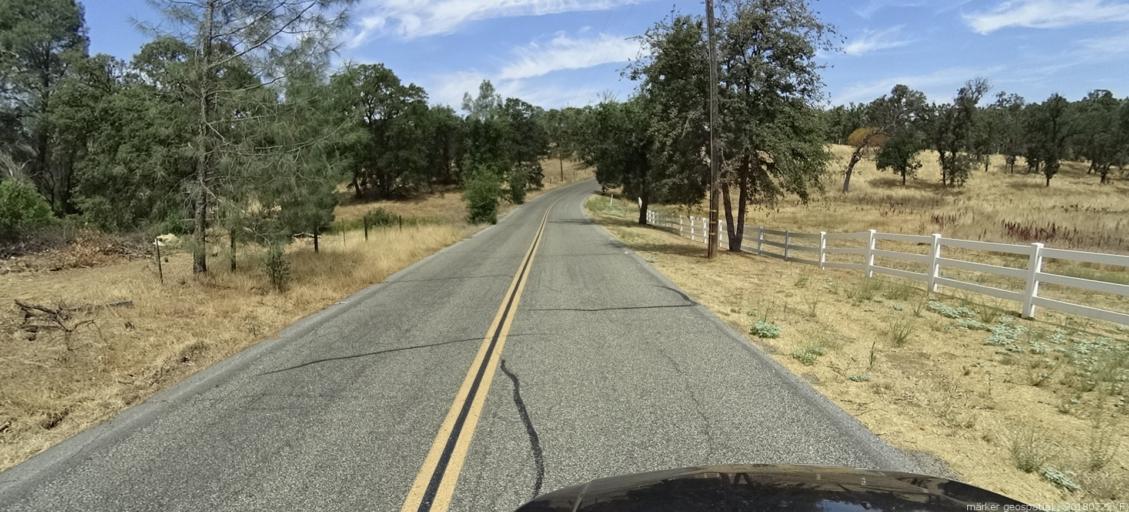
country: US
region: California
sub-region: Madera County
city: Coarsegold
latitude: 37.2715
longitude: -119.7392
